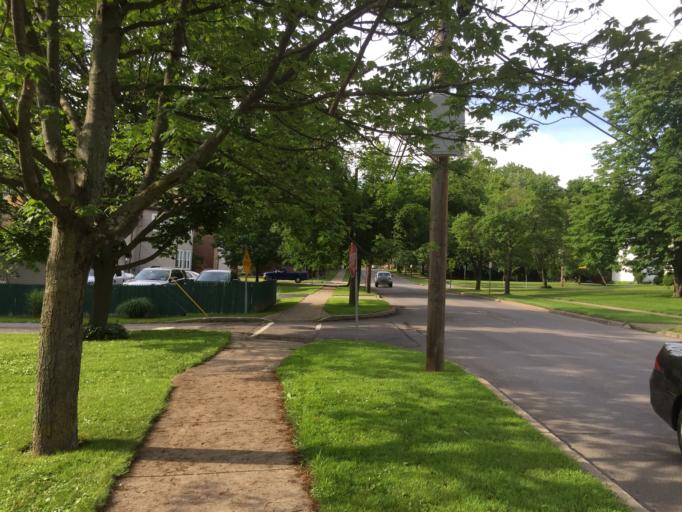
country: US
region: New York
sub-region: Erie County
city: East Aurora
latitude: 42.7649
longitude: -78.6080
